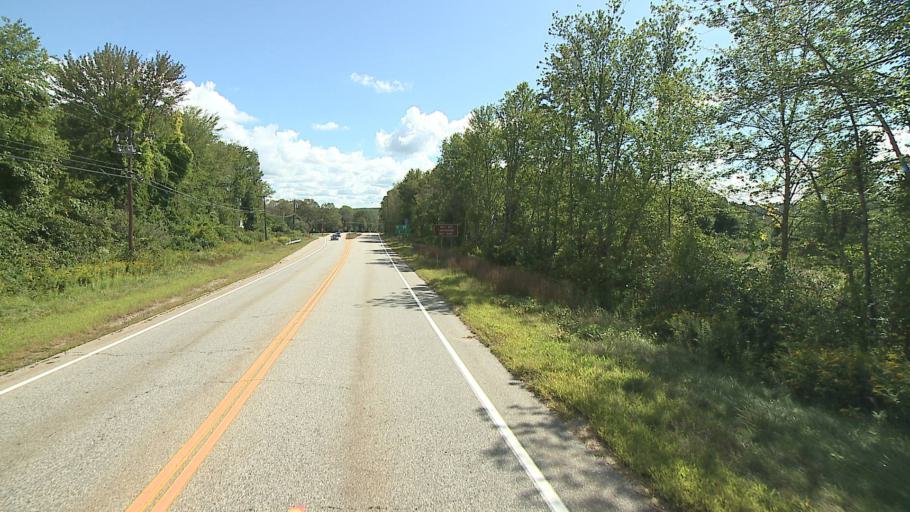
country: US
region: Connecticut
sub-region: Windham County
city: South Woodstock
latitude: 41.8612
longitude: -71.9687
